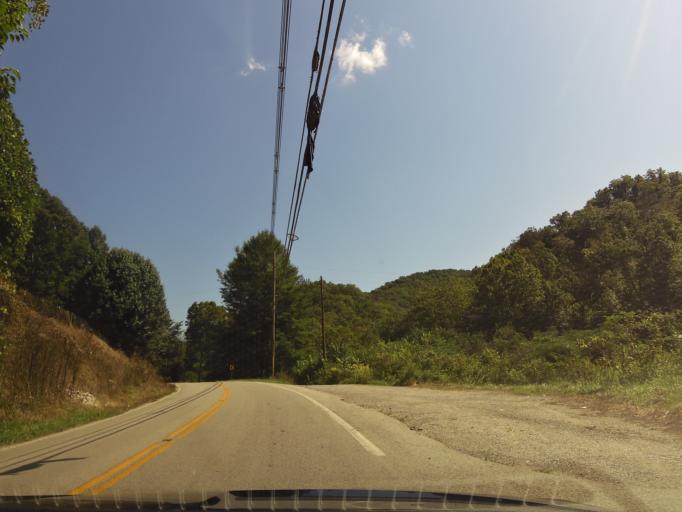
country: US
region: Kentucky
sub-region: Clay County
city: Manchester
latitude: 37.0873
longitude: -83.6778
